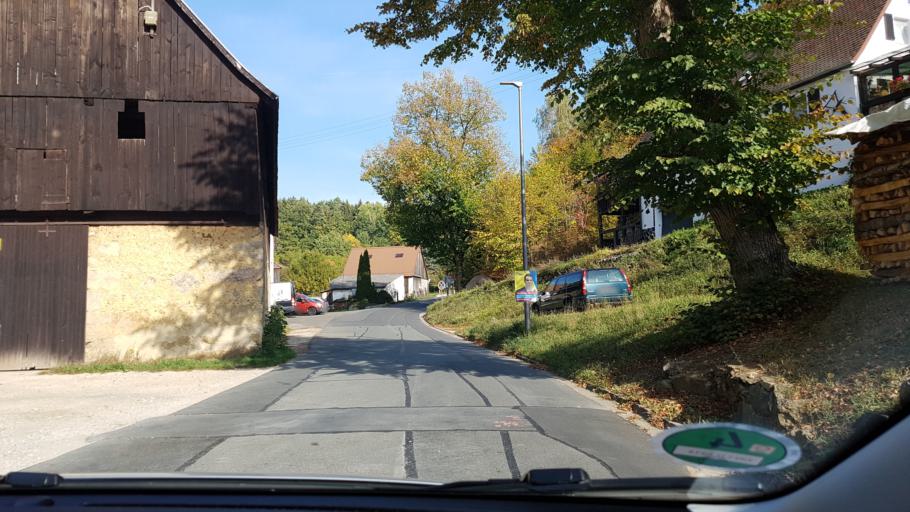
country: DE
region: Bavaria
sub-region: Upper Franconia
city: Waischenfeld
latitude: 49.8136
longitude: 11.3535
